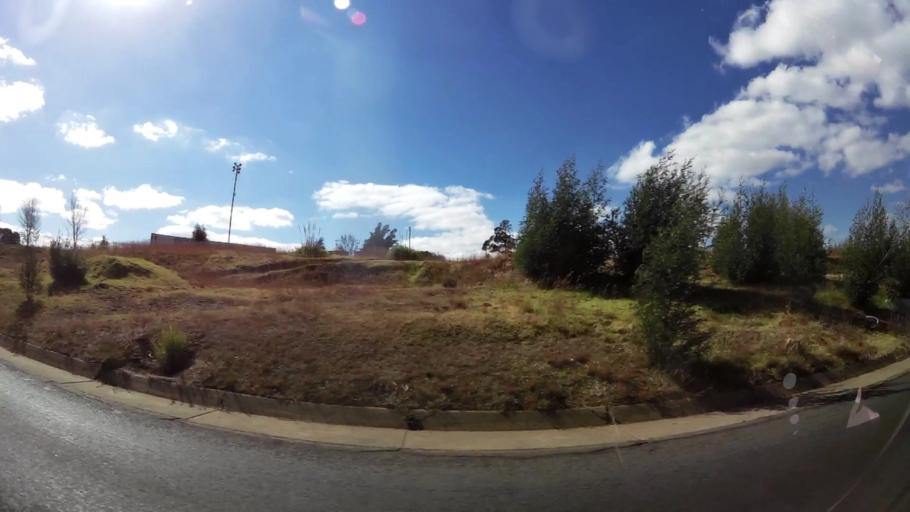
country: ZA
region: Gauteng
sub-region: West Rand District Municipality
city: Krugersdorp
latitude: -26.1084
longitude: 27.8029
